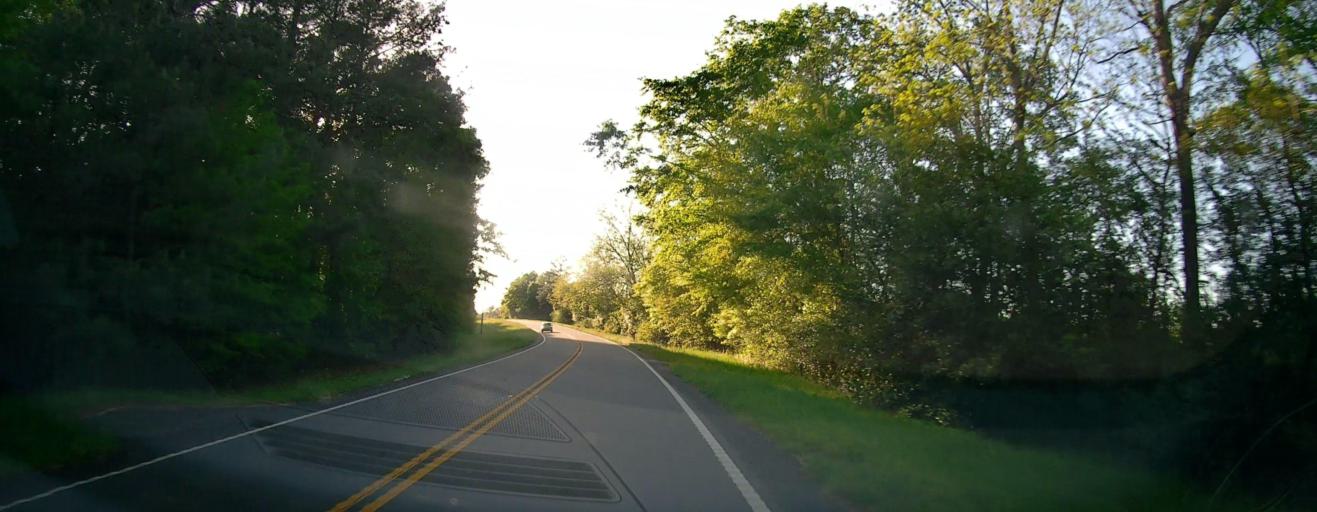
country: US
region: Georgia
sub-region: Schley County
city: Ellaville
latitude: 32.3190
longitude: -84.2598
